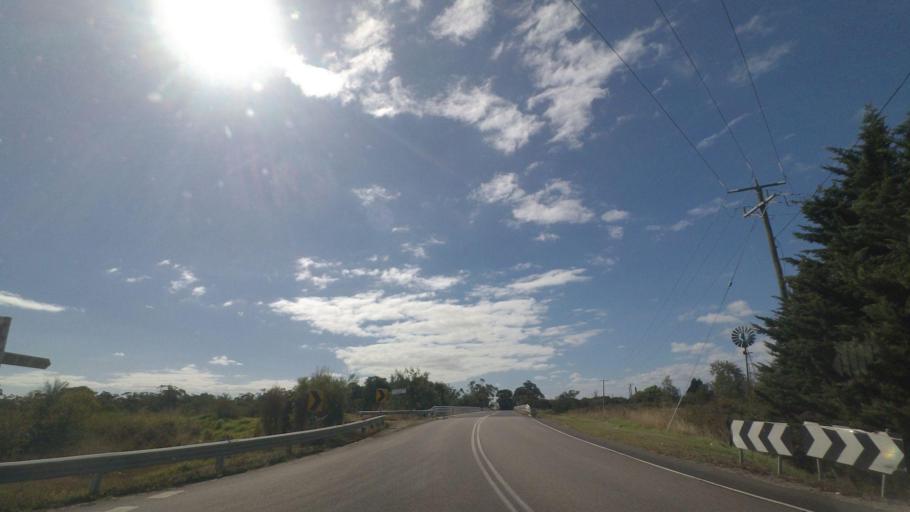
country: AU
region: Victoria
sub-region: Cardinia
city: Pakenham South
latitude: -38.1812
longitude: 145.5739
